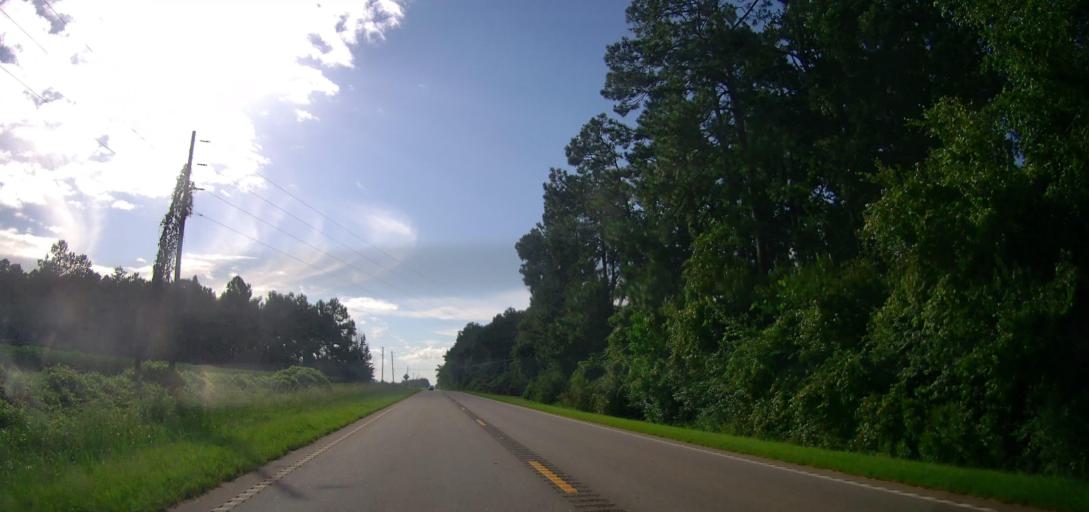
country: US
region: Georgia
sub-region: Coffee County
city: Douglas
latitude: 31.4793
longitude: -82.7914
